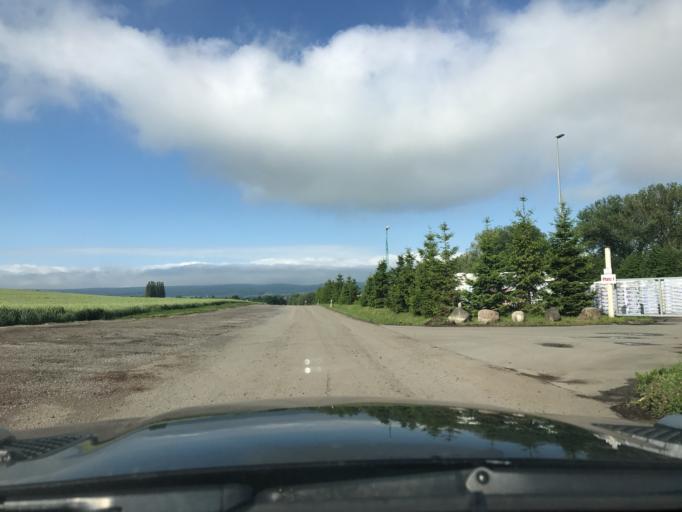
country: DE
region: Thuringia
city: Niederdorla
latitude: 51.1670
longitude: 10.4558
